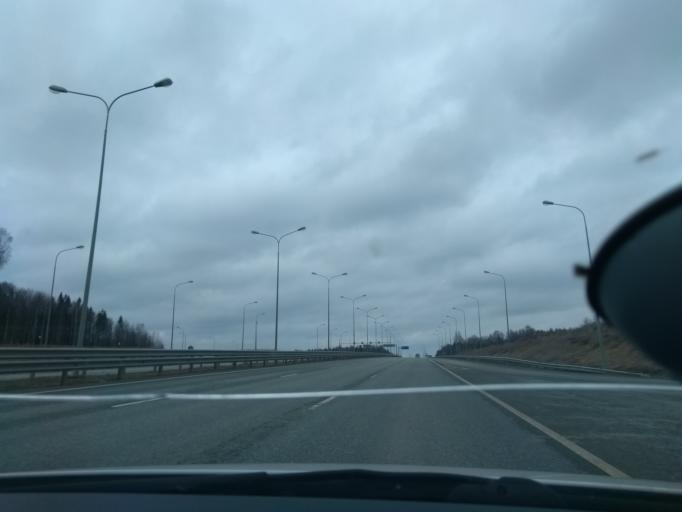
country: RU
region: Perm
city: Zvezdnyy
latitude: 57.7341
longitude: 56.3447
